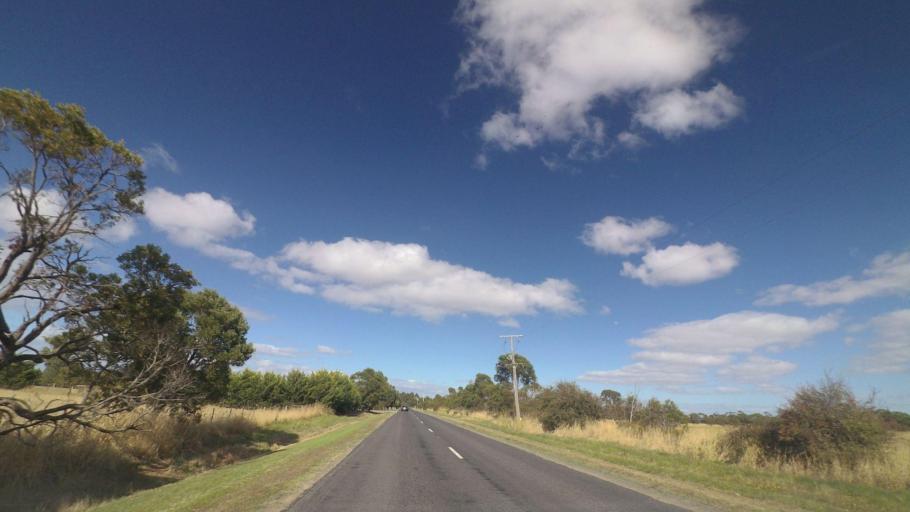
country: AU
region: Victoria
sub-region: Cardinia
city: Koo-Wee-Rup
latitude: -38.1910
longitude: 145.5210
